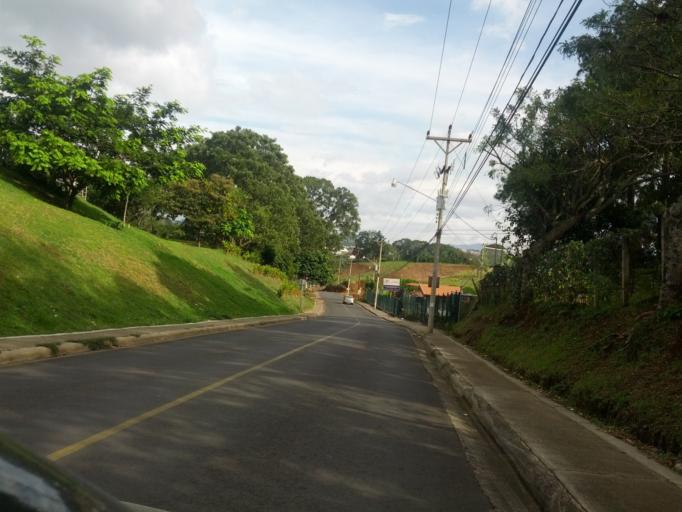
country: CR
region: Heredia
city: Llorente
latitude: 10.0166
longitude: -84.1760
